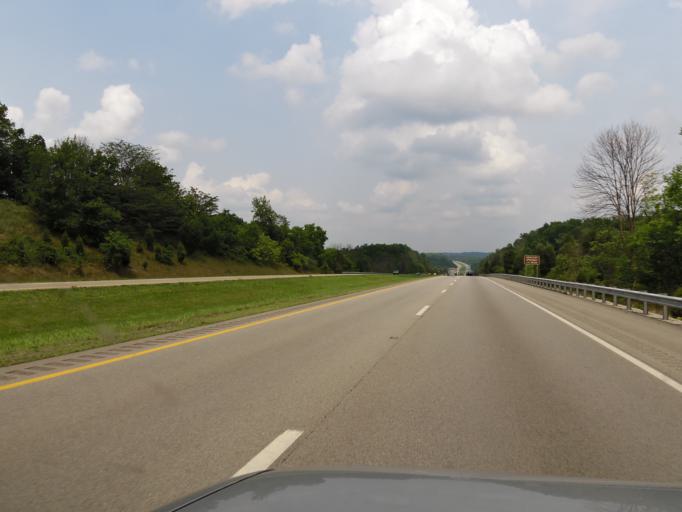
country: US
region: Indiana
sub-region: Switzerland County
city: Vevay
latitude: 38.6792
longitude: -84.9752
